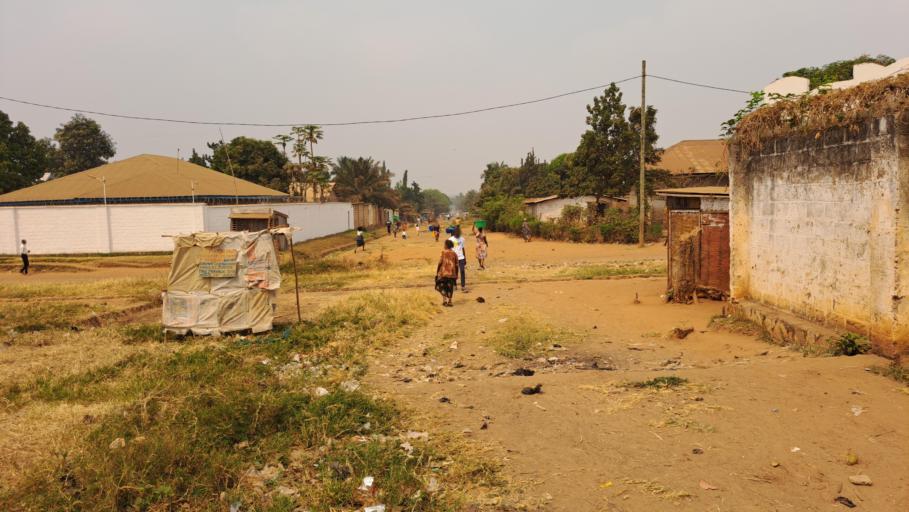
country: CD
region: Kasai-Oriental
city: Mbuji-Mayi
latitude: -6.1191
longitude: 23.6018
